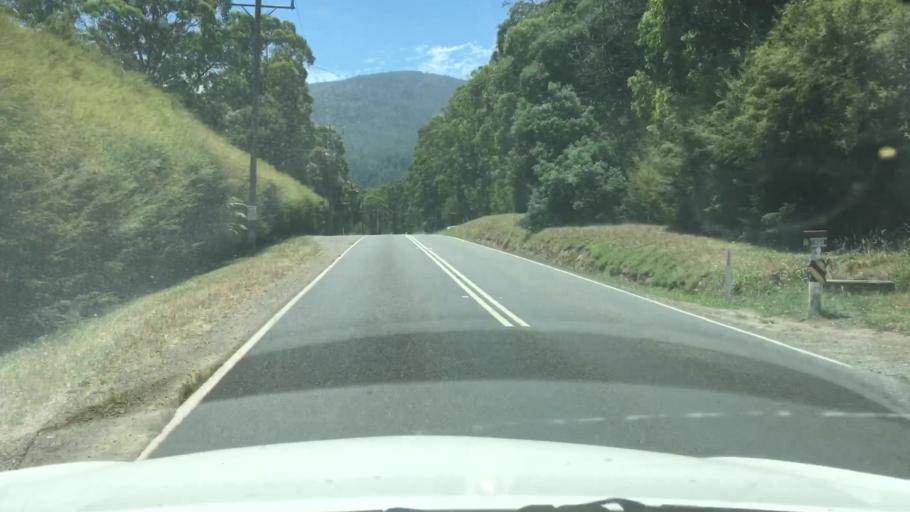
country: AU
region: Victoria
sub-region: Yarra Ranges
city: Millgrove
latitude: -37.7301
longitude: 145.7489
